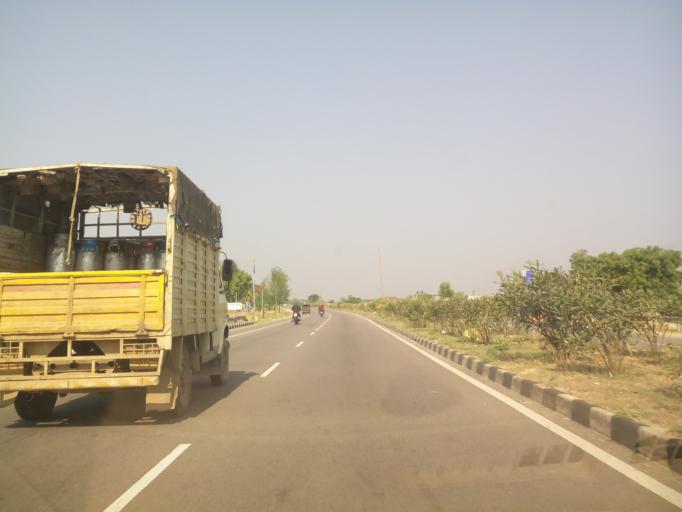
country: IN
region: Karnataka
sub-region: Tumkur
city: Kunigal
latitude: 12.9966
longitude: 76.9279
